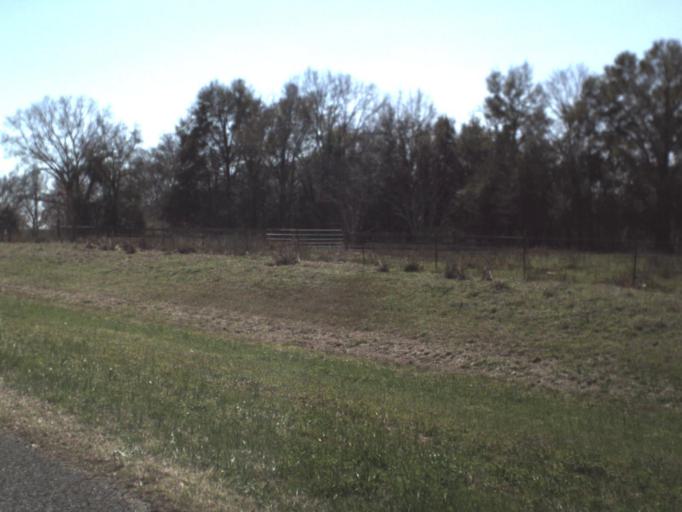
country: US
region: Florida
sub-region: Jackson County
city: Graceville
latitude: 30.8966
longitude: -85.3720
